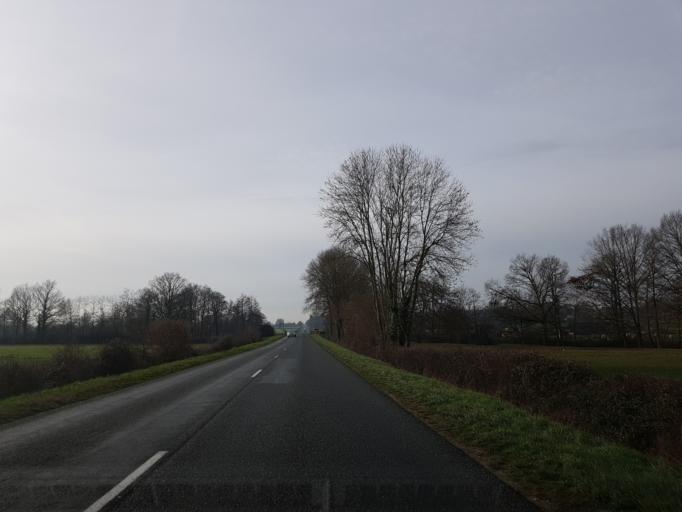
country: FR
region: Auvergne
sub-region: Departement de l'Allier
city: Lusigny
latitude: 46.6011
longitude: 3.5231
